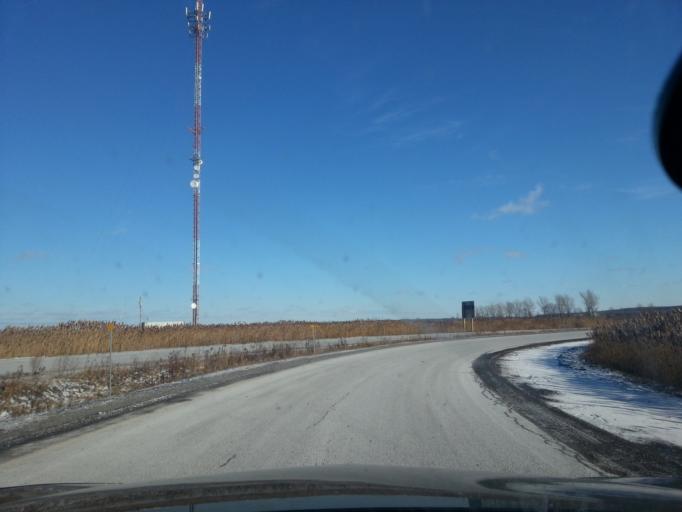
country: CA
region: Ontario
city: Casselman
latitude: 45.3277
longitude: -74.9848
